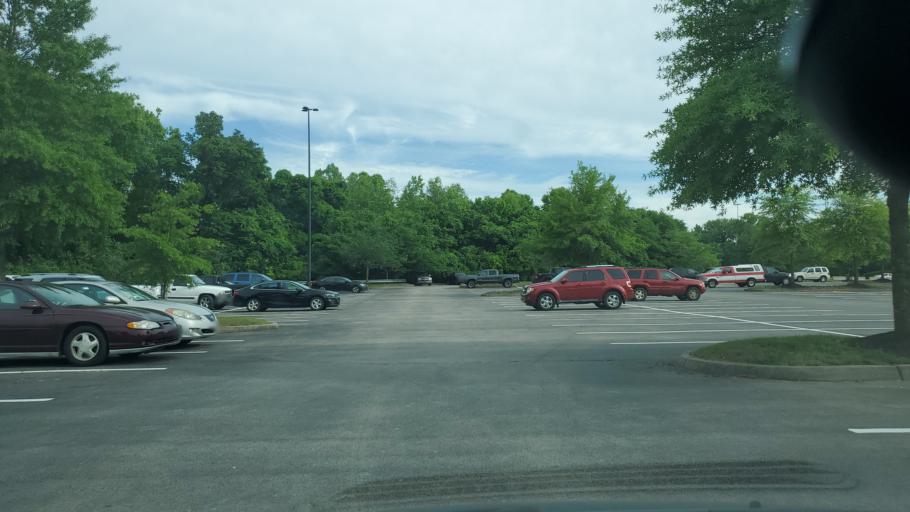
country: US
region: Tennessee
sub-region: Davidson County
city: Lakewood
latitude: 36.1996
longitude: -86.6899
